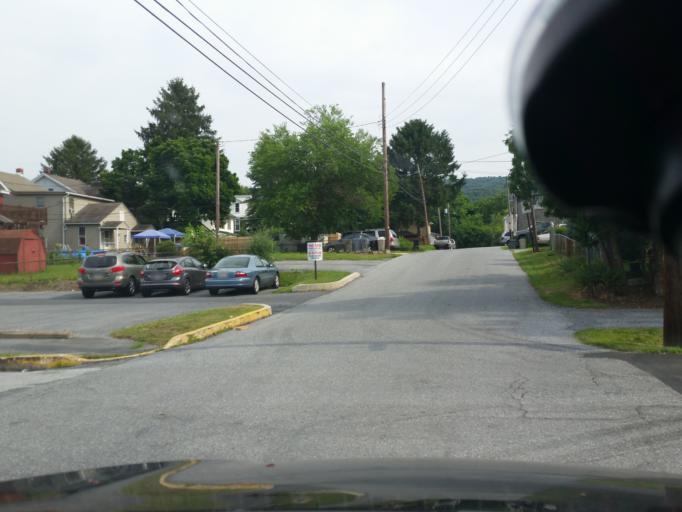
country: US
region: Pennsylvania
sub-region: Perry County
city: Marysville
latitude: 40.3407
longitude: -76.9301
